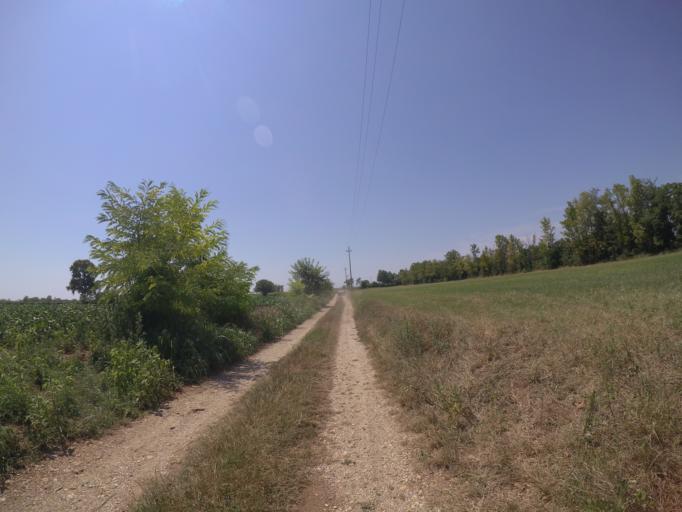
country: IT
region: Friuli Venezia Giulia
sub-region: Provincia di Udine
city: Castions di Strada
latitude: 45.9295
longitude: 13.1867
